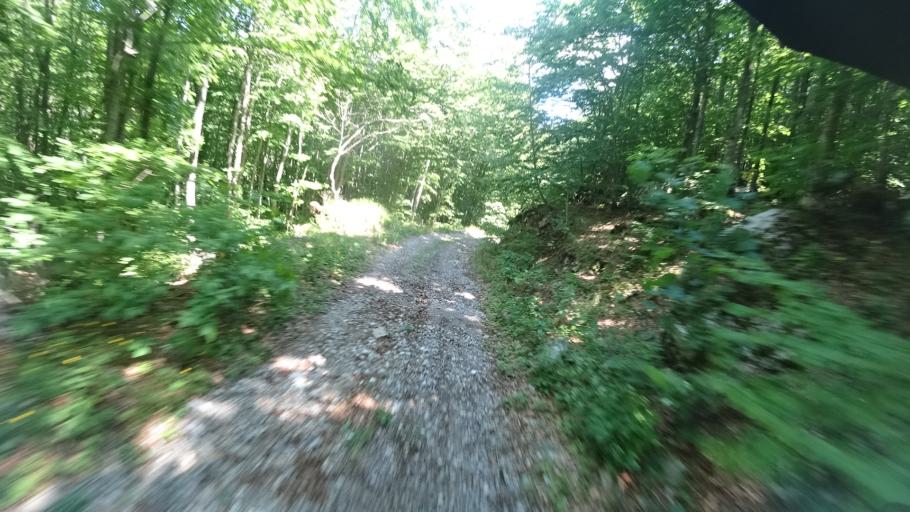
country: HR
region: Zadarska
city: Gracac
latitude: 44.4590
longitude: 15.9058
